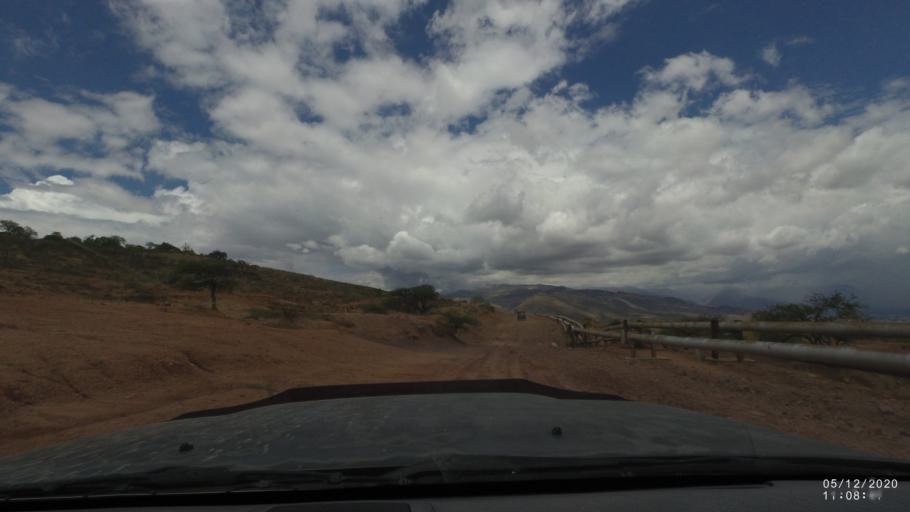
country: BO
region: Cochabamba
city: Sipe Sipe
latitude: -17.5509
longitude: -66.3146
